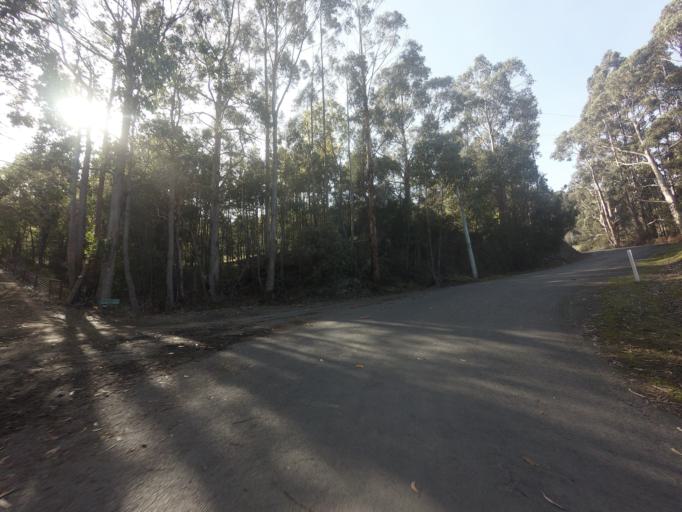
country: AU
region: Tasmania
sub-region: Kingborough
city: Kettering
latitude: -43.1199
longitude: 147.2562
